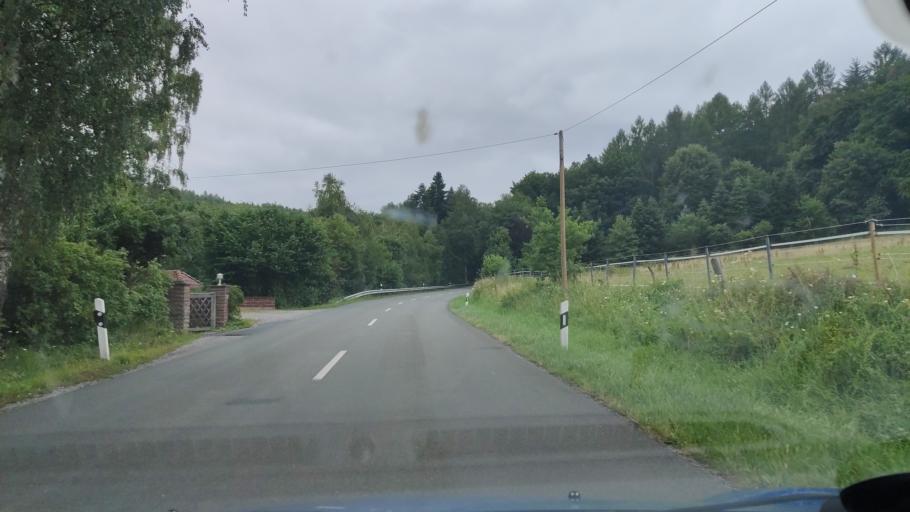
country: DE
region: Lower Saxony
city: Holzminden
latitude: 51.8069
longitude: 9.4784
